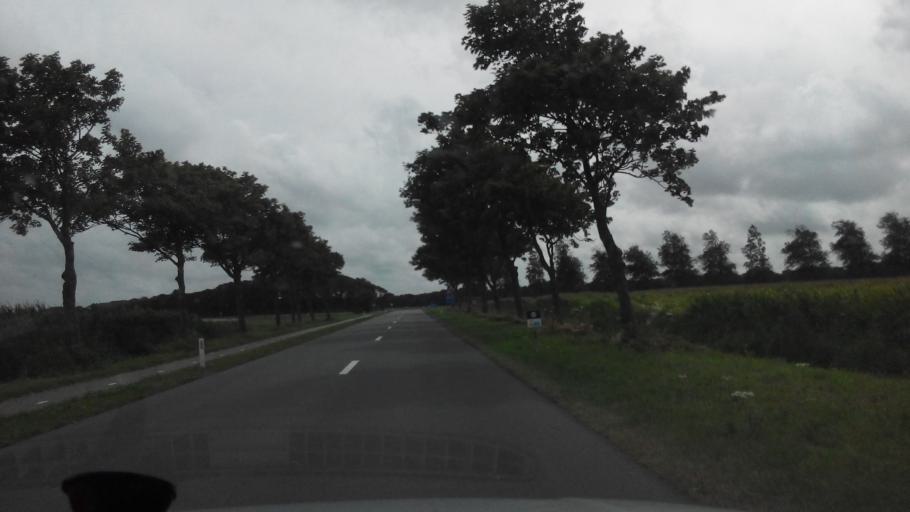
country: NL
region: North Holland
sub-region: Gemeente Hollands Kroon
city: Den Oever
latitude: 52.8838
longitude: 4.9380
